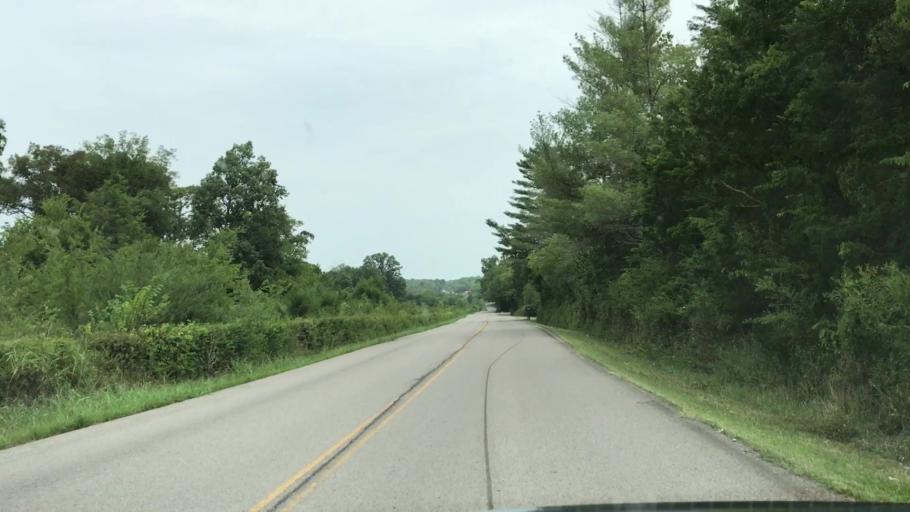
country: US
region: Tennessee
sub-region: Williamson County
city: Nolensville
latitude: 35.9610
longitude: -86.6340
